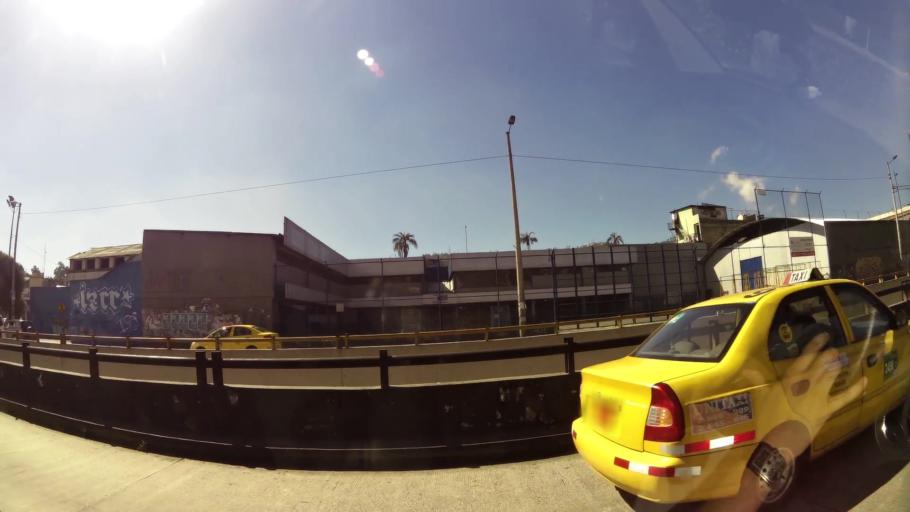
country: EC
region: Pichincha
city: Quito
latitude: -0.2452
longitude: -78.5193
